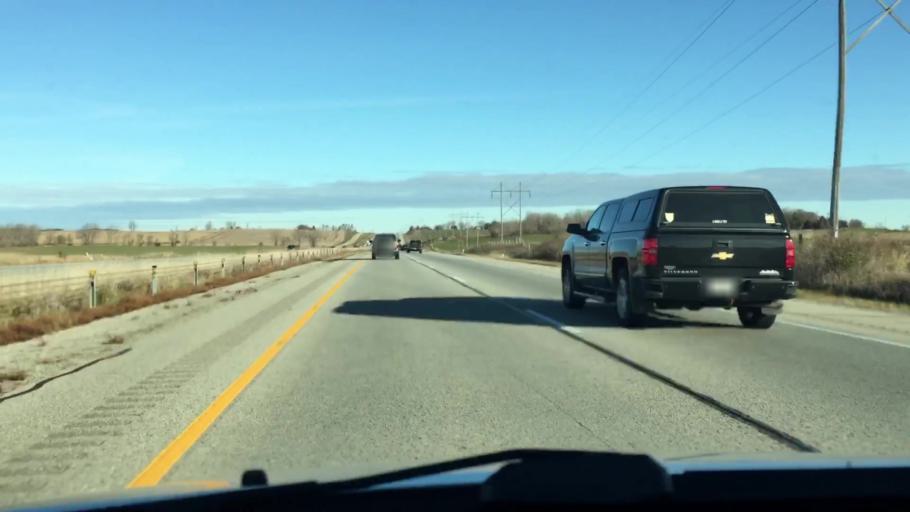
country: US
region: Wisconsin
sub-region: Fond du Lac County
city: Rosendale
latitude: 43.8786
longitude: -88.5840
